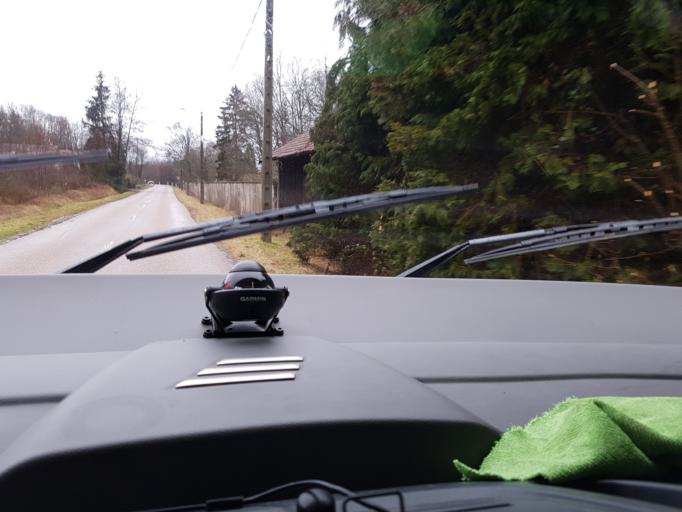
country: FR
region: Lorraine
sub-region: Departement des Vosges
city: Saint-Michel-sur-Meurthe
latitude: 48.3030
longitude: 6.9137
